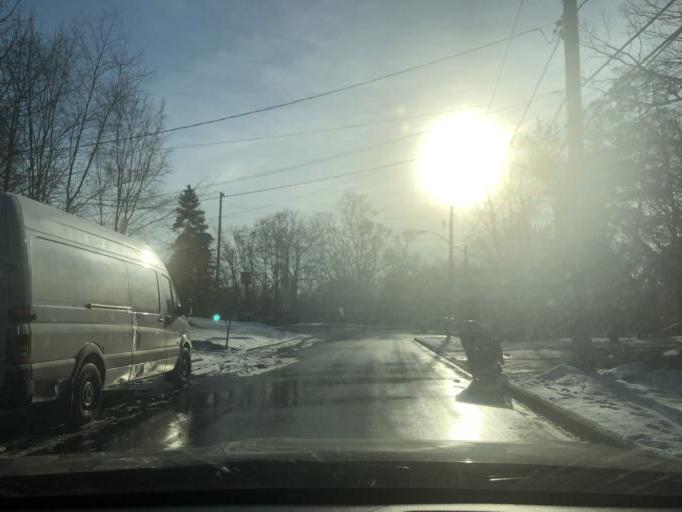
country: CA
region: Ontario
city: Toronto
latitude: 43.6941
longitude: -79.4836
